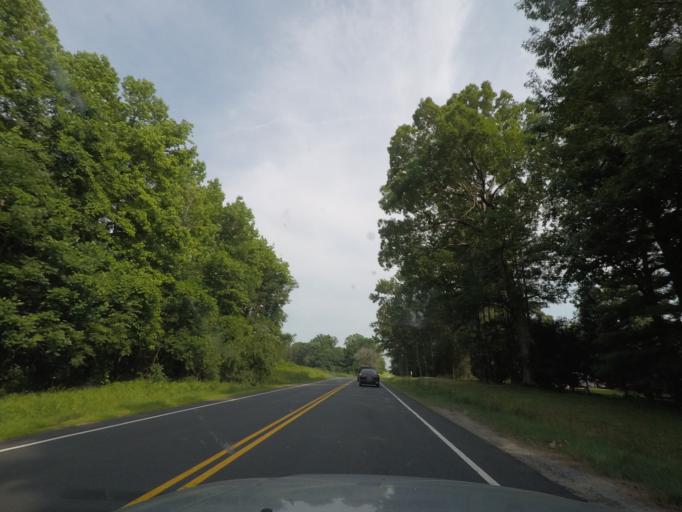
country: US
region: Virginia
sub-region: Prince Edward County
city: Hampden Sydney
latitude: 37.2000
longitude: -78.4325
